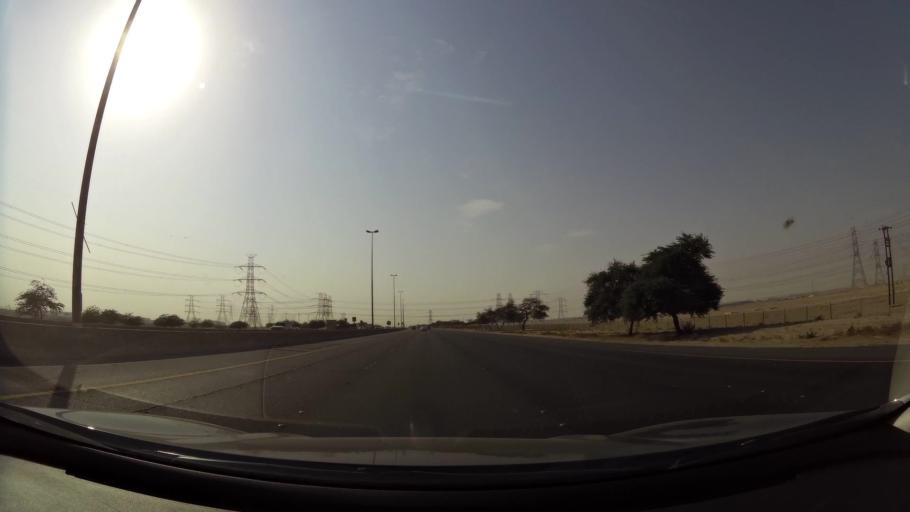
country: KW
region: Al Ahmadi
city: Al Ahmadi
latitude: 29.0170
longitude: 48.0923
